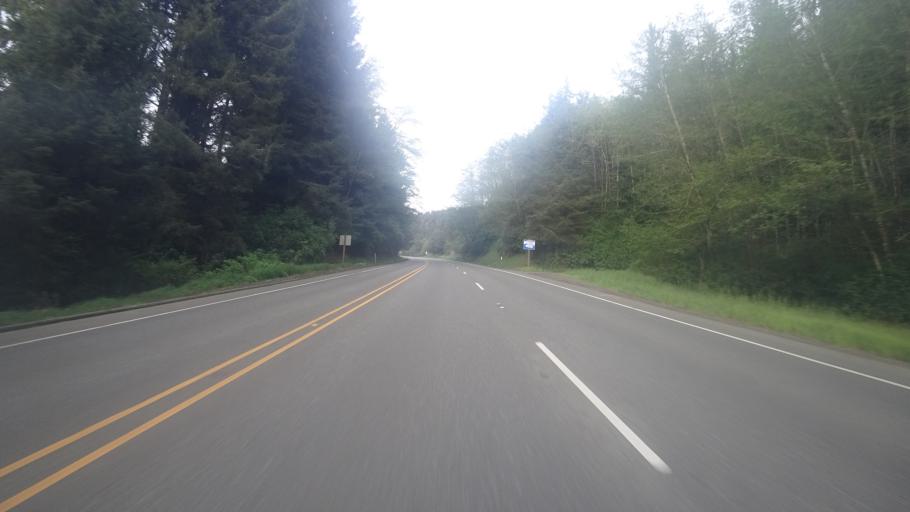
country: US
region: Oregon
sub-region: Douglas County
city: Reedsport
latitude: 43.6724
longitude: -124.1795
